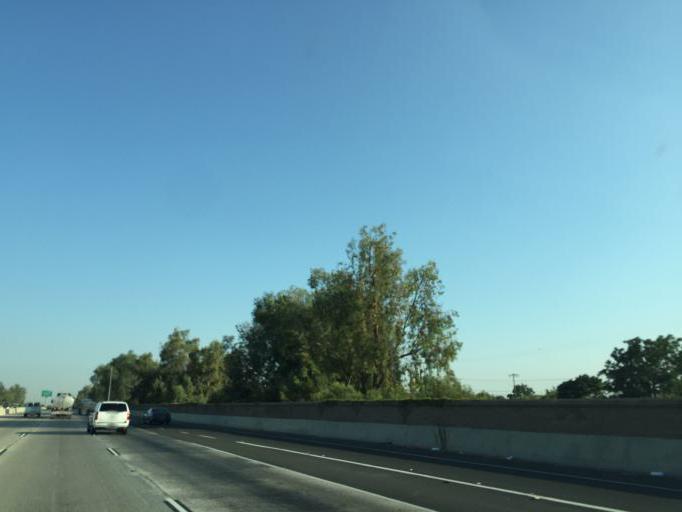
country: US
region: California
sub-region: Fresno County
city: Selma
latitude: 36.5664
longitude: -119.6184
